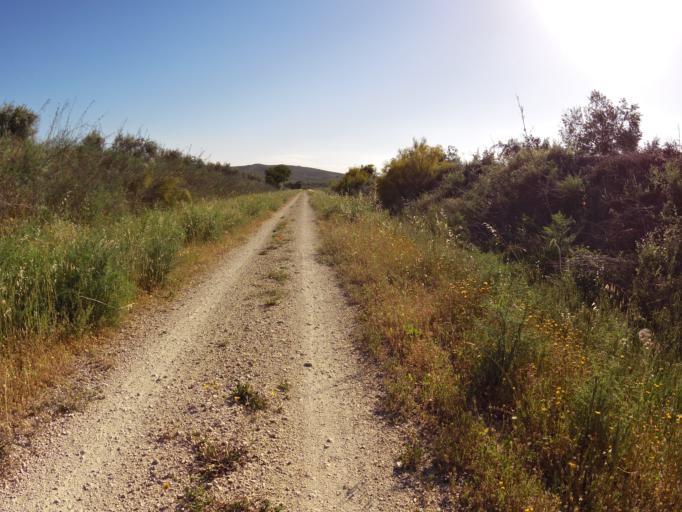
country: ES
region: Andalusia
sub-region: Province of Cordoba
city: Luque
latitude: 37.5749
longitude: -4.2206
